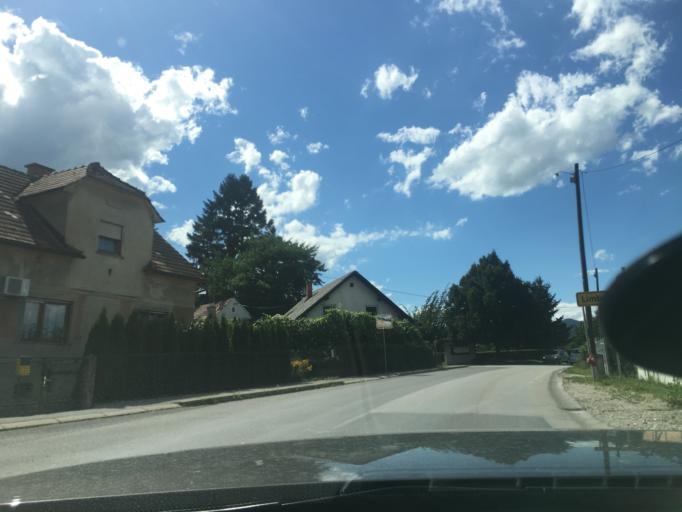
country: SI
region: Maribor
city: Pekre
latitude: 46.5494
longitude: 15.5898
